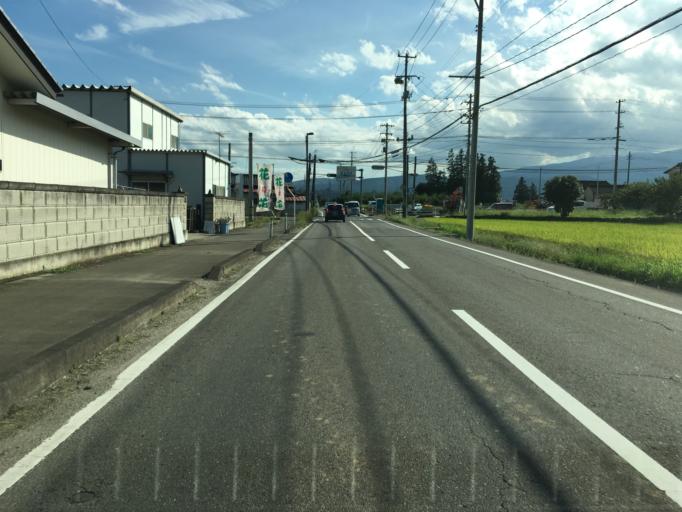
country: JP
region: Fukushima
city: Fukushima-shi
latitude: 37.7588
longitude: 140.4201
